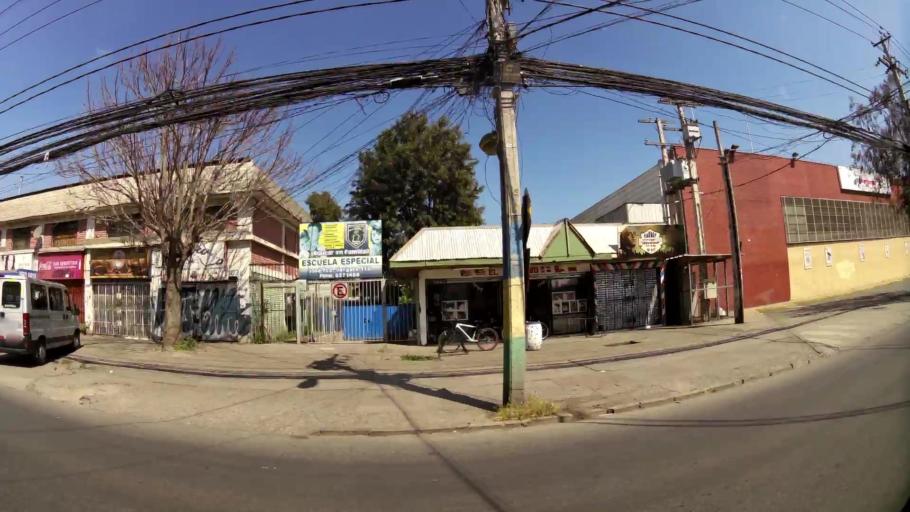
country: CL
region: Santiago Metropolitan
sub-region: Provincia de Santiago
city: Lo Prado
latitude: -33.3669
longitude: -70.7351
